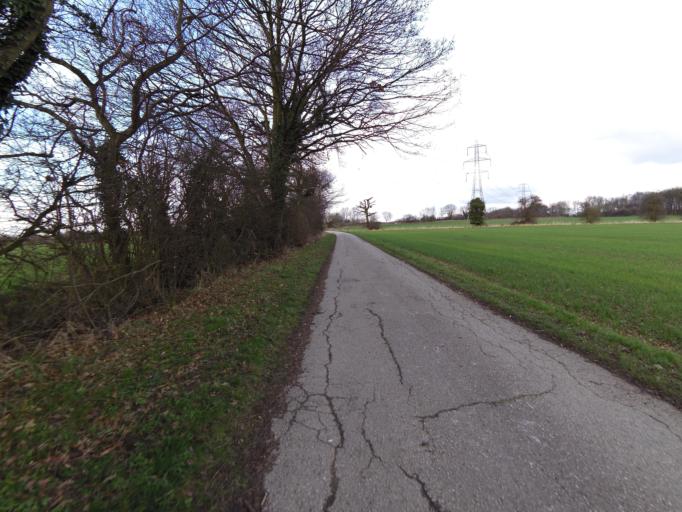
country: GB
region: England
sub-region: East Riding of Yorkshire
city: Pollington
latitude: 53.6604
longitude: -1.0585
